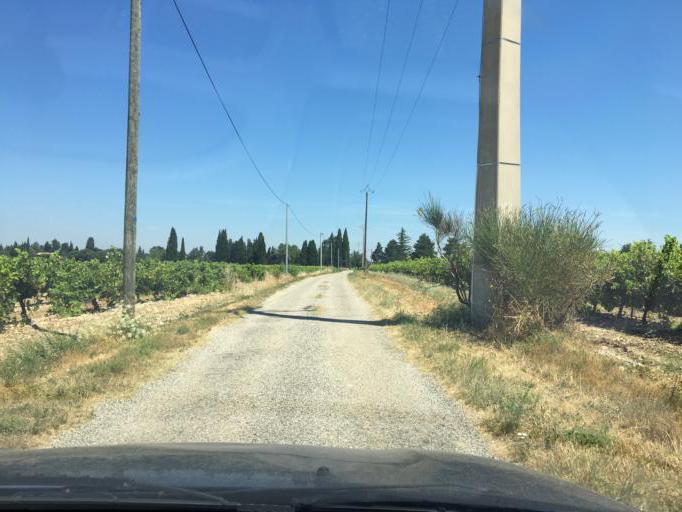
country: FR
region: Provence-Alpes-Cote d'Azur
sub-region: Departement du Vaucluse
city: Camaret-sur-Aigues
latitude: 44.1718
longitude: 4.8951
